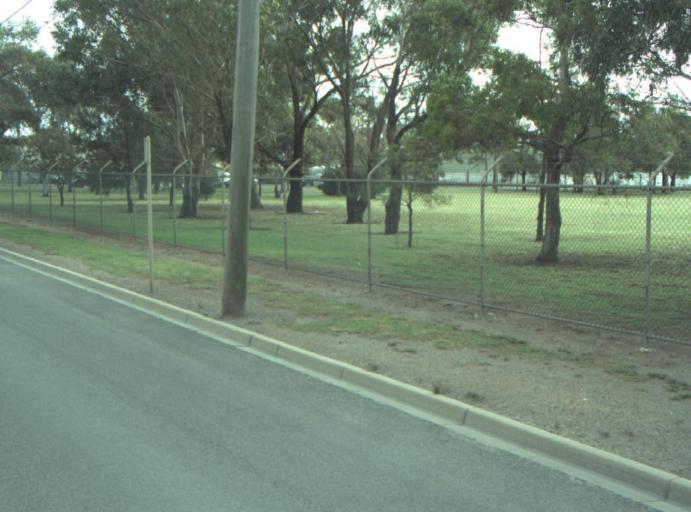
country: AU
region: Victoria
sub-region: Greater Geelong
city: Bell Park
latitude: -38.0889
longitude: 144.3763
